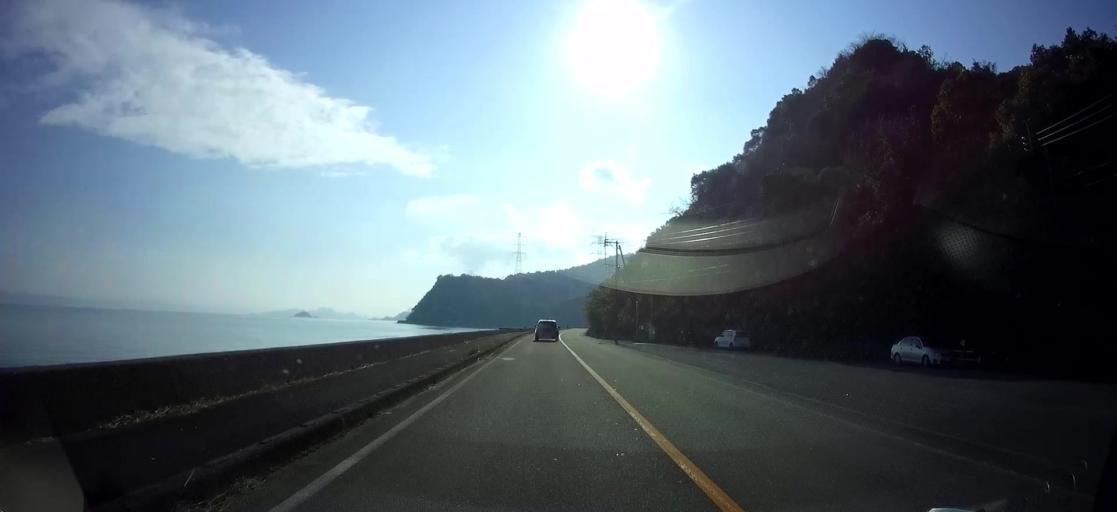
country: JP
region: Kumamoto
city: Yatsushiro
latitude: 32.5141
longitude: 130.4554
